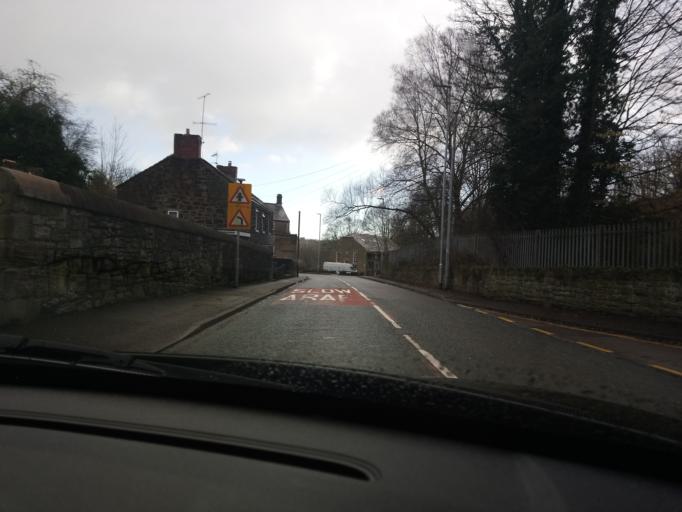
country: GB
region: Wales
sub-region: Wrexham
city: Chirk
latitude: 52.9670
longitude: -3.0667
